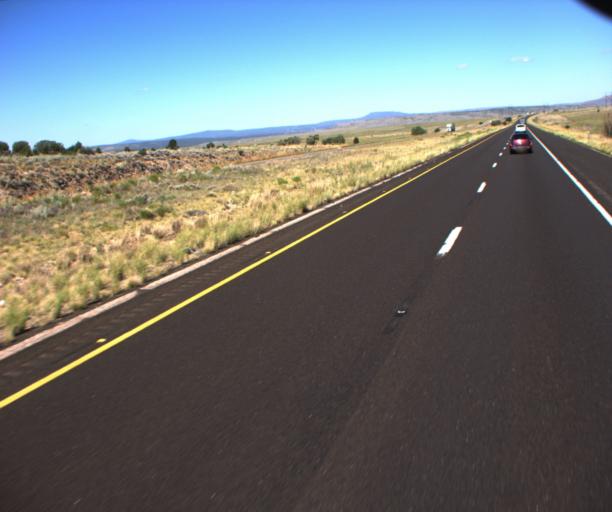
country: US
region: Arizona
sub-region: Yavapai County
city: Paulden
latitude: 35.2863
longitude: -112.8052
